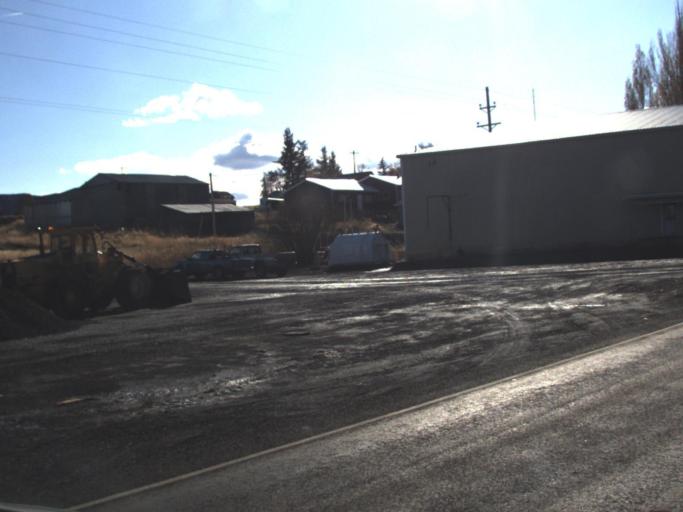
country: US
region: Washington
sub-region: Asotin County
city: Asotin
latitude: 46.1361
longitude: -117.1318
